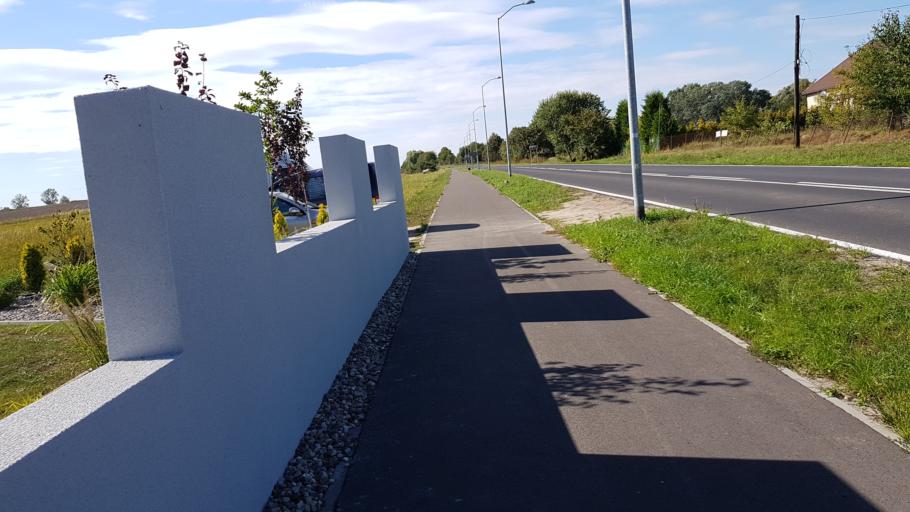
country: PL
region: West Pomeranian Voivodeship
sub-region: Powiat policki
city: Przeclaw
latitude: 53.3521
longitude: 14.4706
